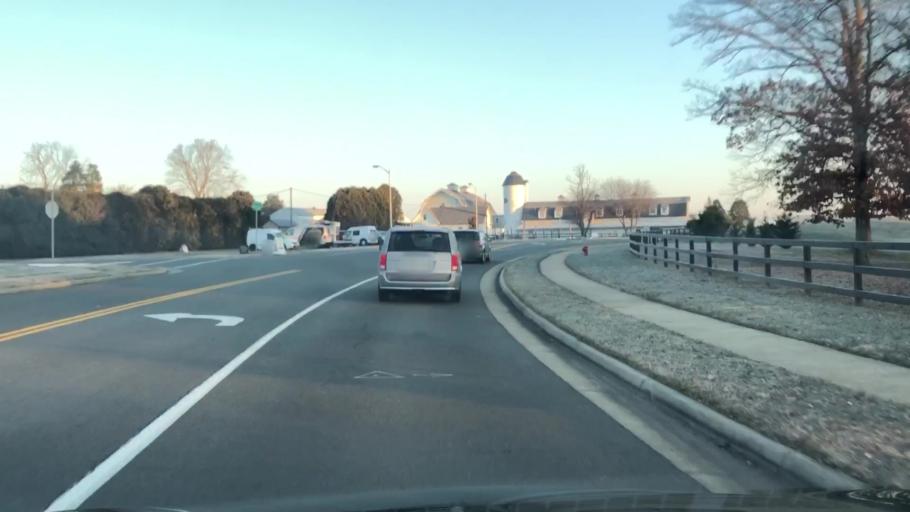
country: US
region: Virginia
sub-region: Fauquier County
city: New Baltimore
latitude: 38.7413
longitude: -77.6763
